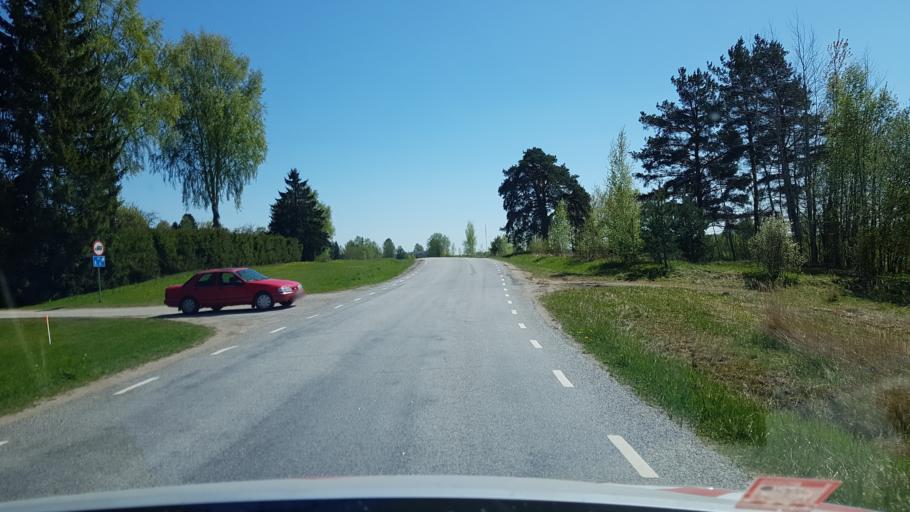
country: EE
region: Vorumaa
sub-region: Voru linn
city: Voru
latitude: 57.9075
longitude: 26.9772
